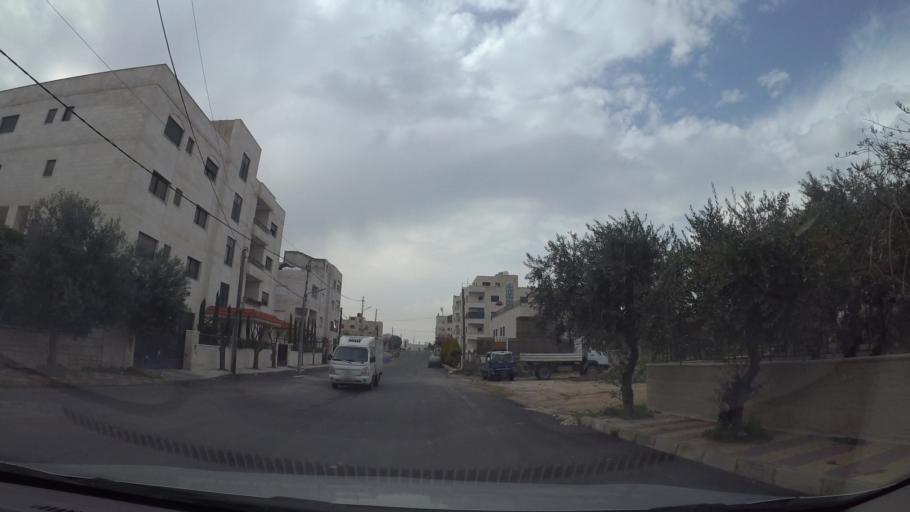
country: JO
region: Amman
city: Umm as Summaq
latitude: 31.8812
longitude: 35.8611
